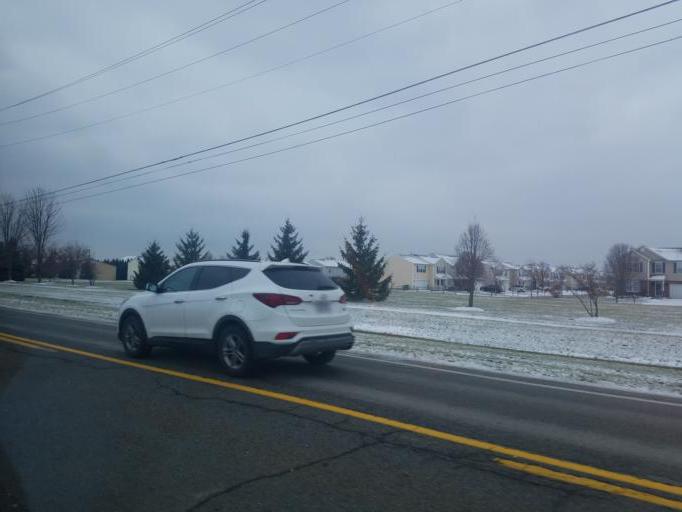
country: US
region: Ohio
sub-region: Franklin County
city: Reynoldsburg
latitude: 40.0125
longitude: -82.7903
